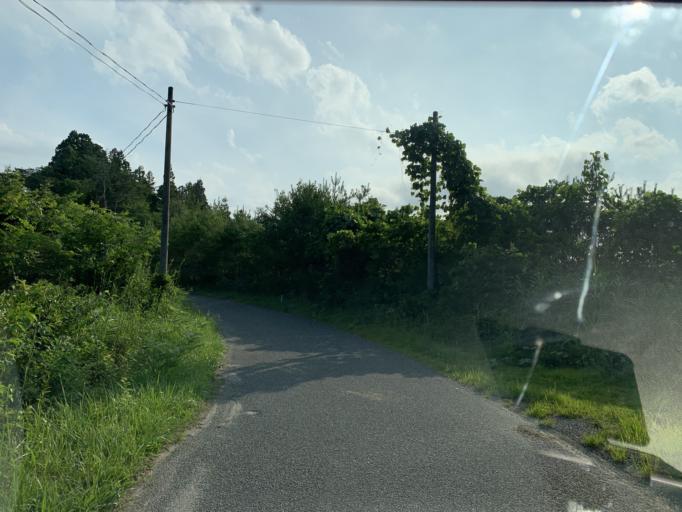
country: JP
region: Iwate
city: Ichinoseki
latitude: 38.8610
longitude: 141.1191
